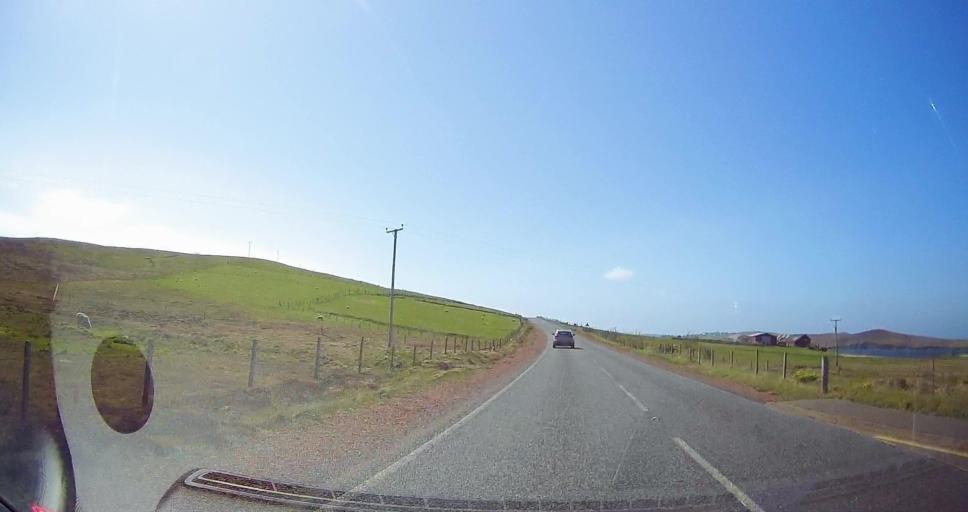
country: GB
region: Scotland
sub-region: Shetland Islands
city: Sandwick
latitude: 60.1173
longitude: -1.2922
